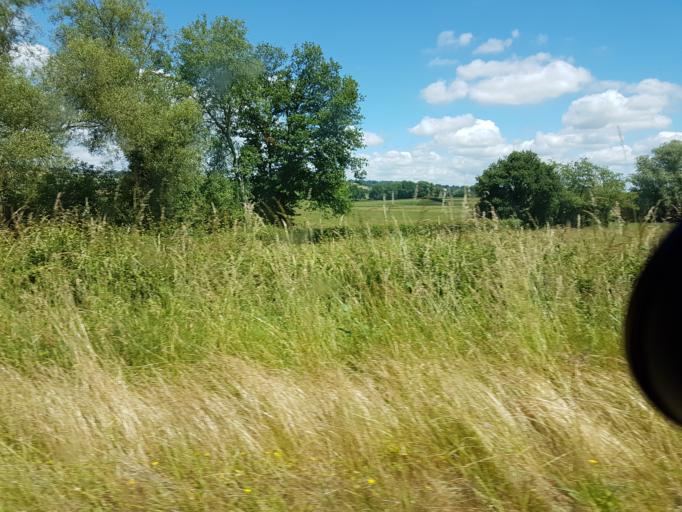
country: FR
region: Bourgogne
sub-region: Departement de Saone-et-Loire
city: Curgy
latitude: 47.0297
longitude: 4.4189
